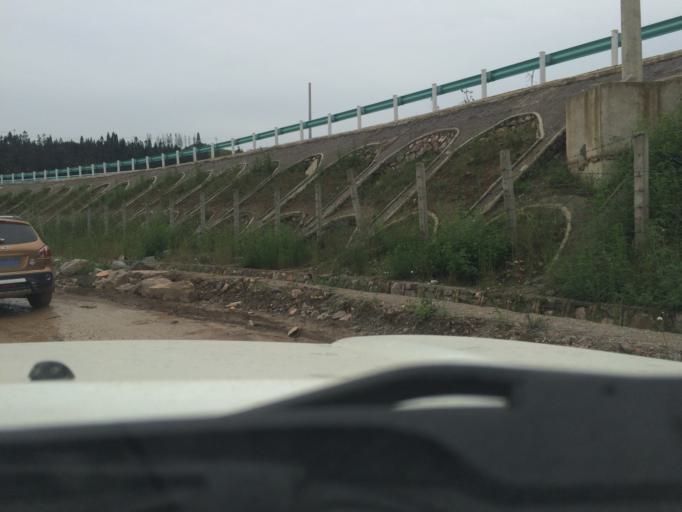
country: CN
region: Guizhou Sheng
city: Zhongshan
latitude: 26.6191
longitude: 106.2635
